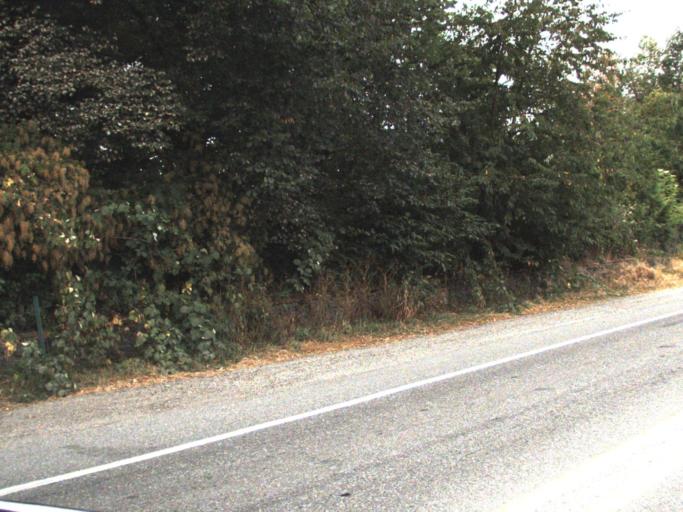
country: US
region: Washington
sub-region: King County
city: Fall City
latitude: 47.5698
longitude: -121.8946
